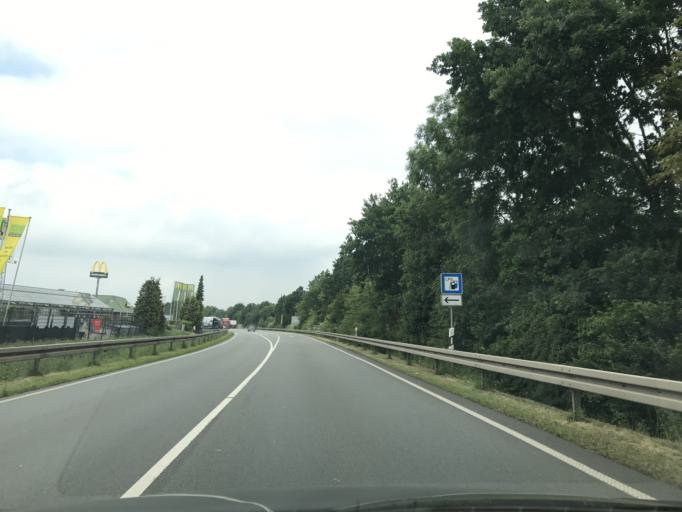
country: DE
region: Lower Saxony
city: Bassum
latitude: 52.8597
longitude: 8.7501
